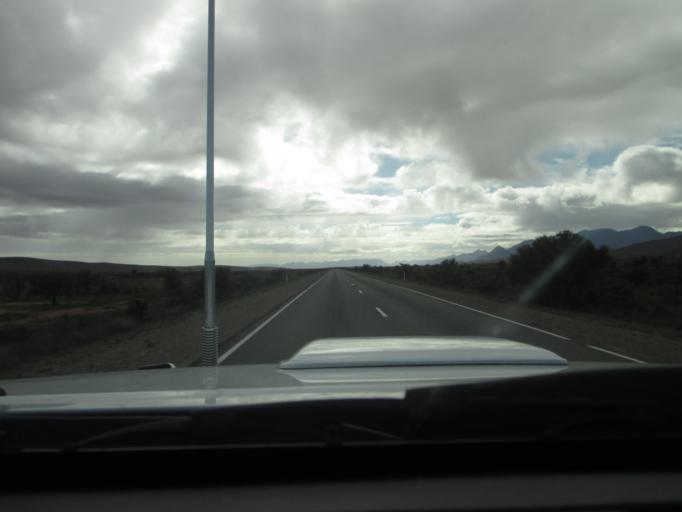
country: AU
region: South Australia
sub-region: Flinders Ranges
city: Quorn
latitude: -31.6188
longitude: 138.3943
